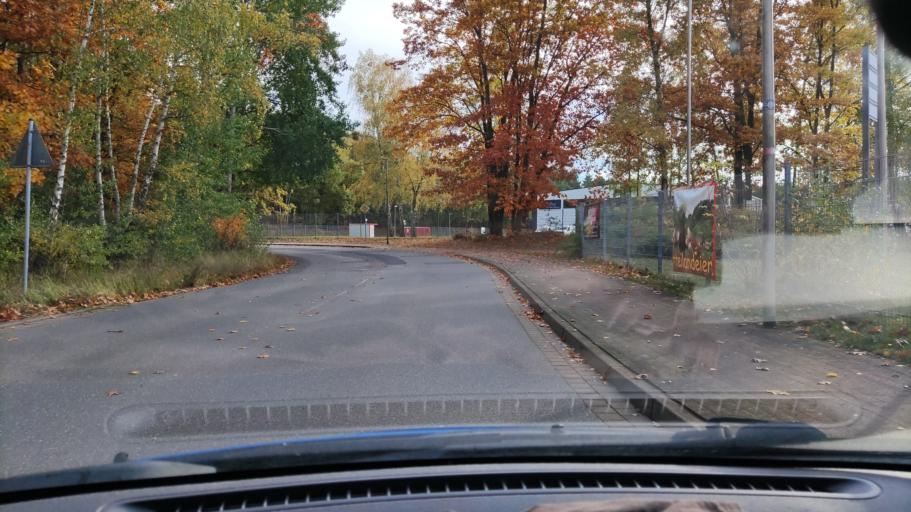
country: DE
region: Mecklenburg-Vorpommern
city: Ludwigslust
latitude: 53.3106
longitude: 11.5125
